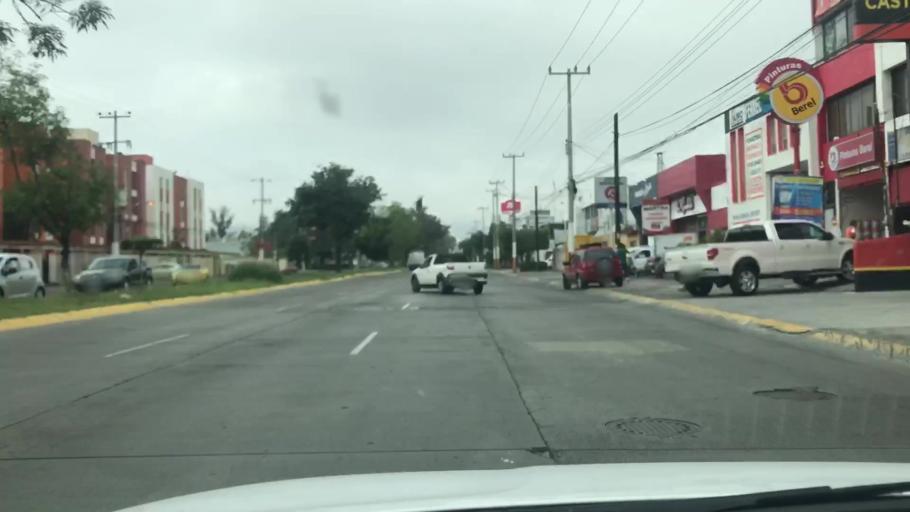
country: MX
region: Jalisco
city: Guadalajara
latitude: 20.6351
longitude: -103.4245
